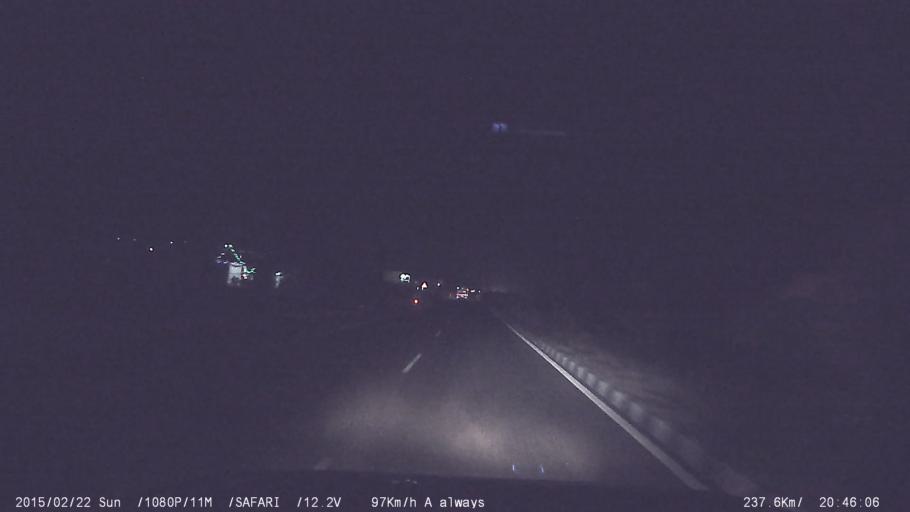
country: IN
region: Tamil Nadu
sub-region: Dindigul
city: Vedasandur
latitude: 10.4784
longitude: 77.9479
